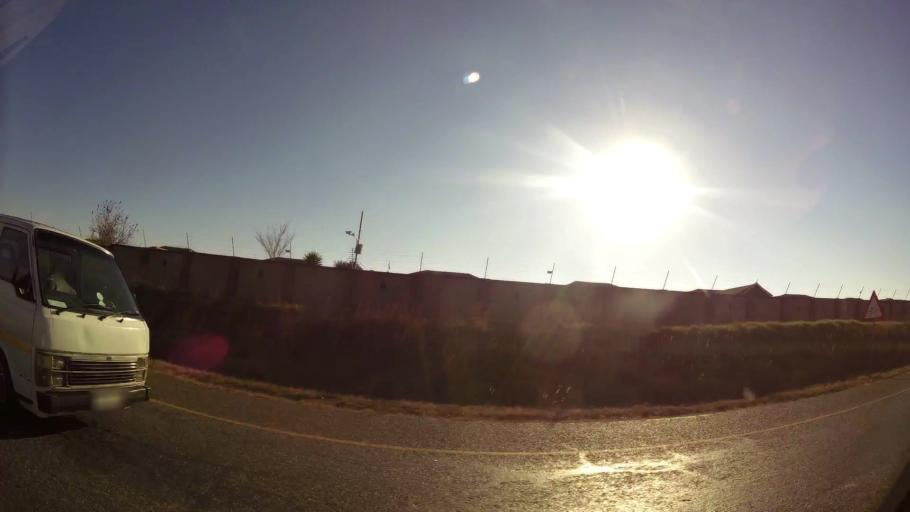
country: ZA
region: Gauteng
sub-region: Ekurhuleni Metropolitan Municipality
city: Germiston
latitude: -26.3543
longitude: 28.1065
